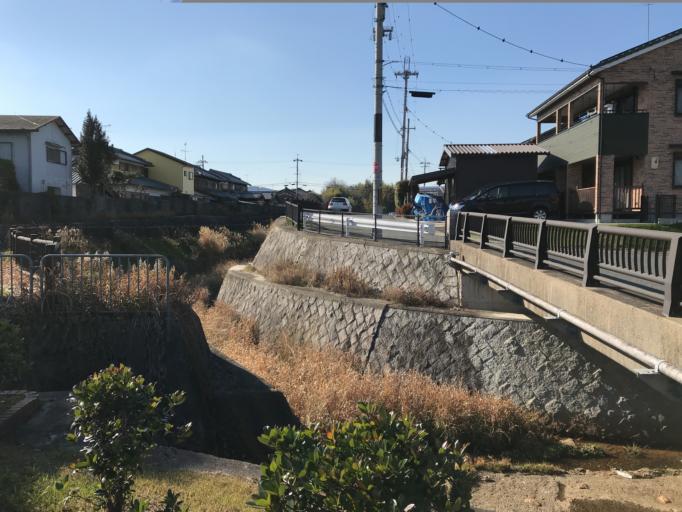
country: JP
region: Kyoto
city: Tanabe
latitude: 34.8176
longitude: 135.7765
